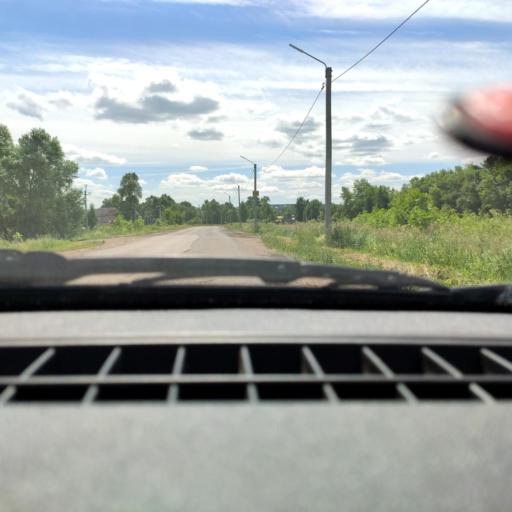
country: RU
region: Bashkortostan
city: Ufa
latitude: 54.6559
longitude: 56.0614
